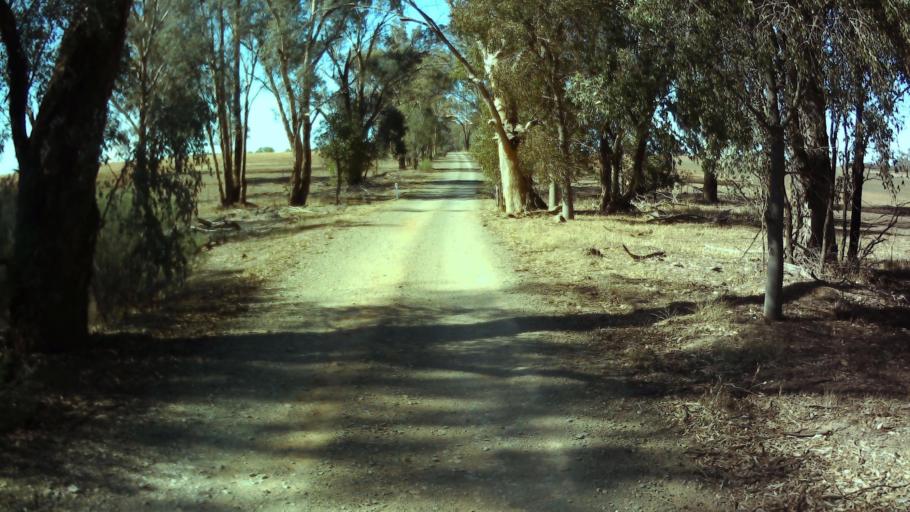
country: AU
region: New South Wales
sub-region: Weddin
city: Grenfell
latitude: -33.7440
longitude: 147.8313
